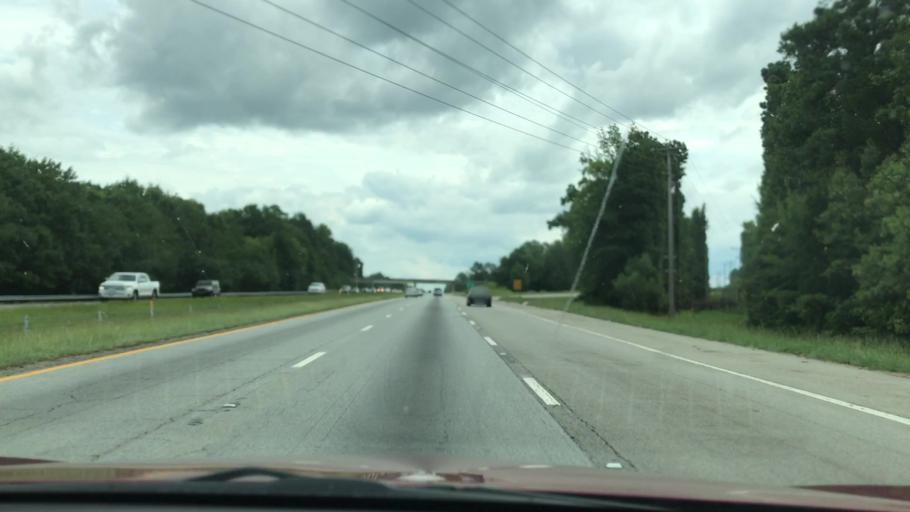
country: US
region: South Carolina
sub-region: Richland County
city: Lake Murray of Richland
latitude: 34.1476
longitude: -81.2418
